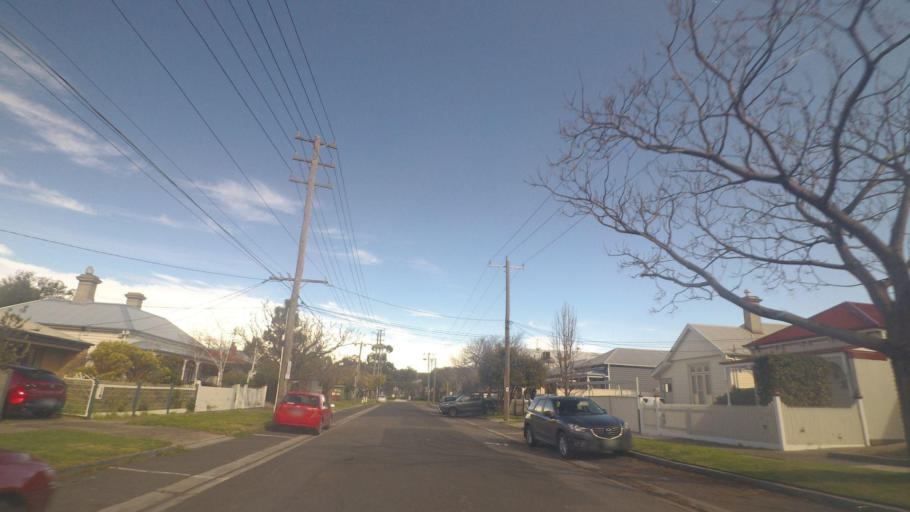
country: AU
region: Victoria
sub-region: Hobsons Bay
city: Spotswood
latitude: -37.8308
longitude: 144.8882
